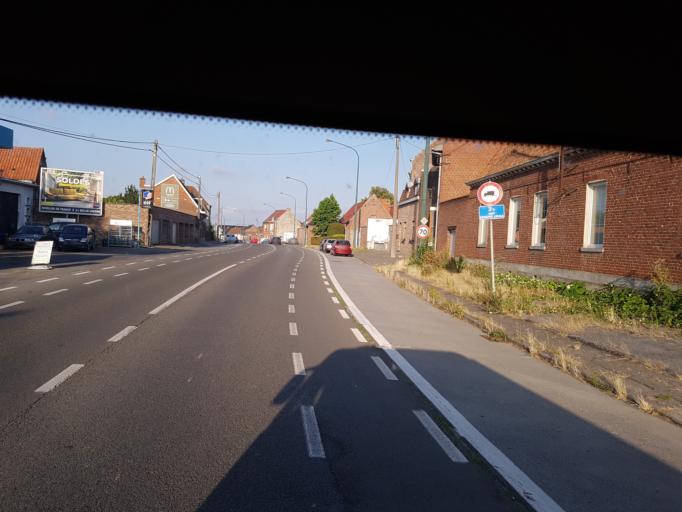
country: BE
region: Wallonia
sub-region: Province du Hainaut
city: Tournai
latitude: 50.6037
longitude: 3.3465
